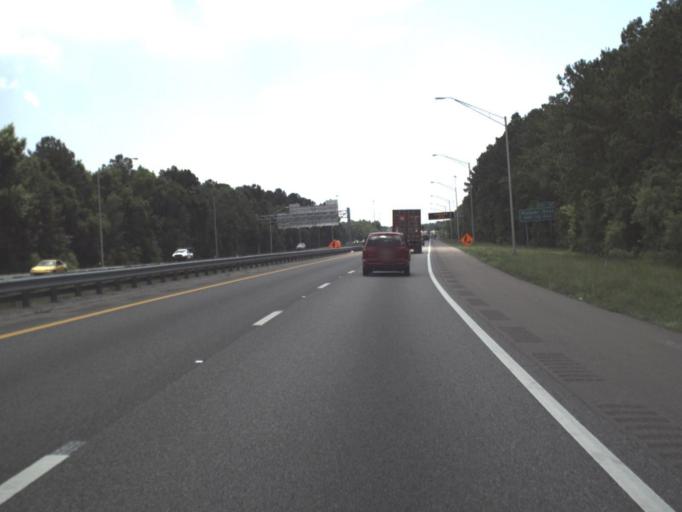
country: US
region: Florida
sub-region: Duval County
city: Jacksonville
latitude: 30.4543
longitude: -81.6229
